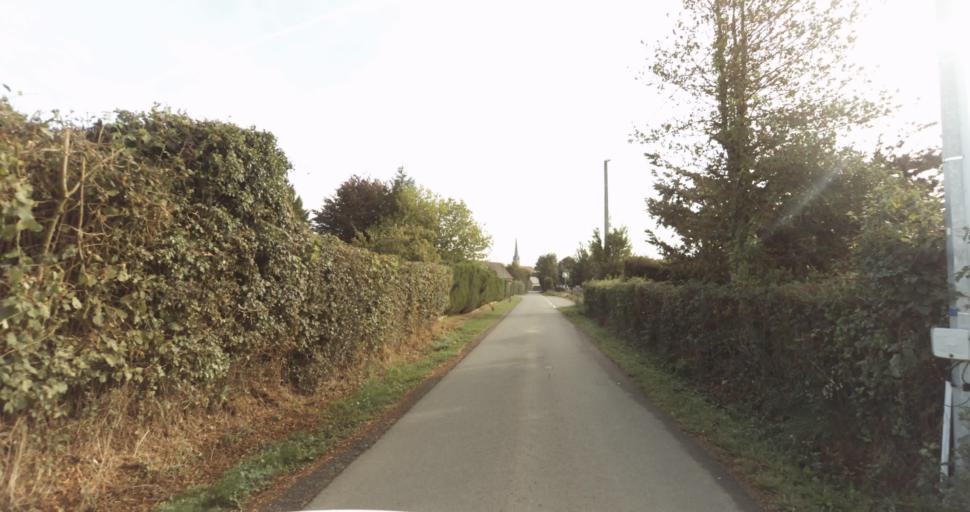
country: FR
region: Lower Normandy
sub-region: Departement de l'Orne
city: Vimoutiers
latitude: 48.9125
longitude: 0.3024
